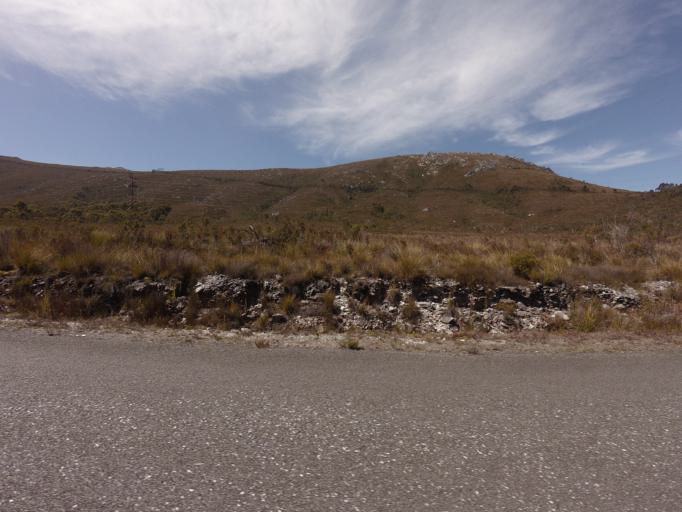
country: AU
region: Tasmania
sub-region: West Coast
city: Queenstown
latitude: -42.7896
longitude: 146.0628
